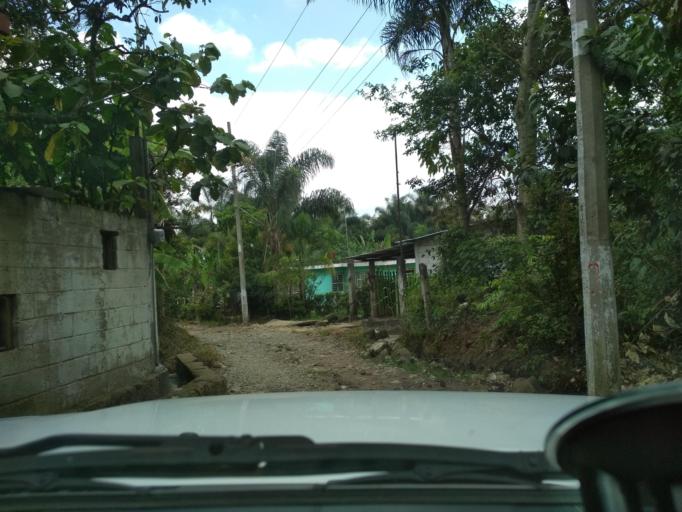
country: MX
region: Veracruz
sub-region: Fortin
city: Monte Salas
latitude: 18.9373
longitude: -97.0154
